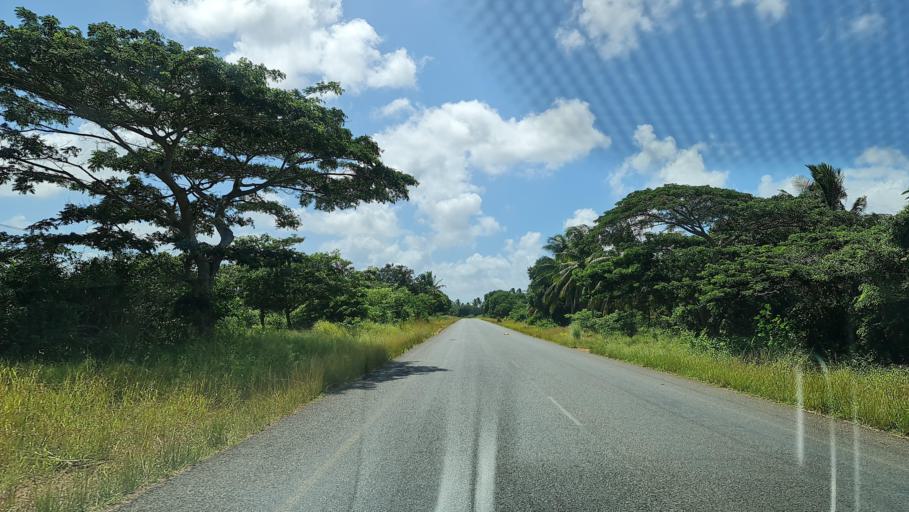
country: MZ
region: Inhambane
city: Maxixe
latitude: -24.5403
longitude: 34.9283
